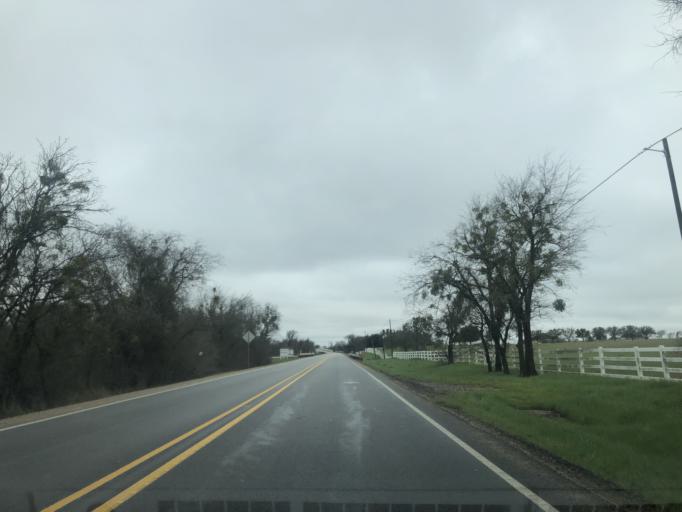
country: US
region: Texas
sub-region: Williamson County
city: Hutto
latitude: 30.6302
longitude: -97.5440
